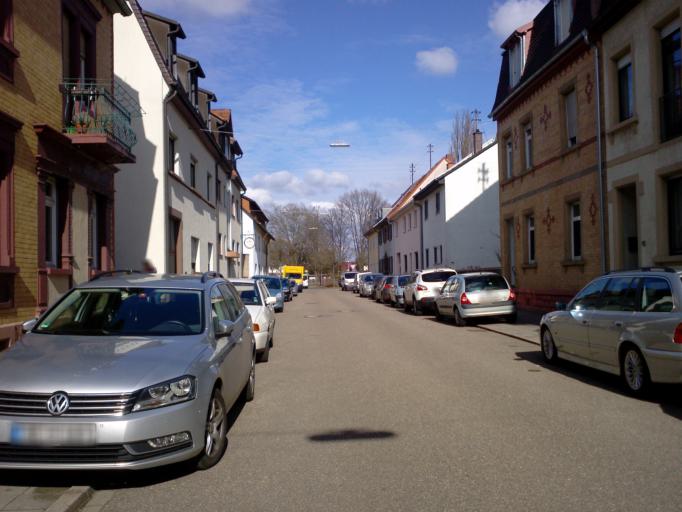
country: DE
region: Baden-Wuerttemberg
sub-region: Karlsruhe Region
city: Karlsruhe
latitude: 48.9875
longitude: 8.3788
